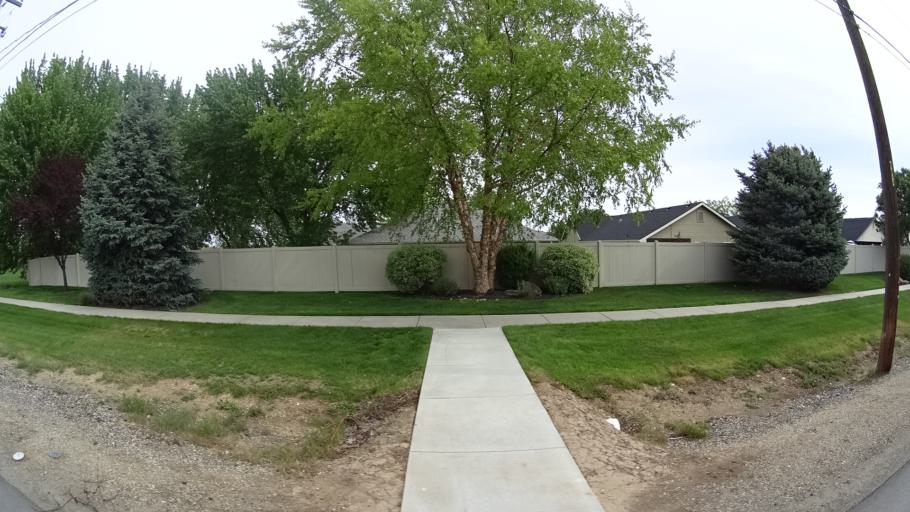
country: US
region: Idaho
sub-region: Ada County
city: Garden City
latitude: 43.5465
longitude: -116.3039
